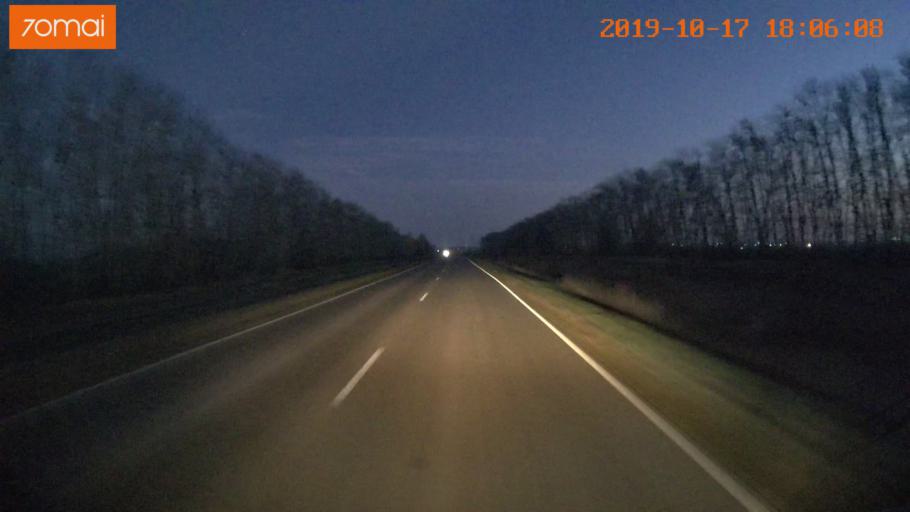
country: RU
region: Tula
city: Kurkino
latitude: 53.4554
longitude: 38.6526
